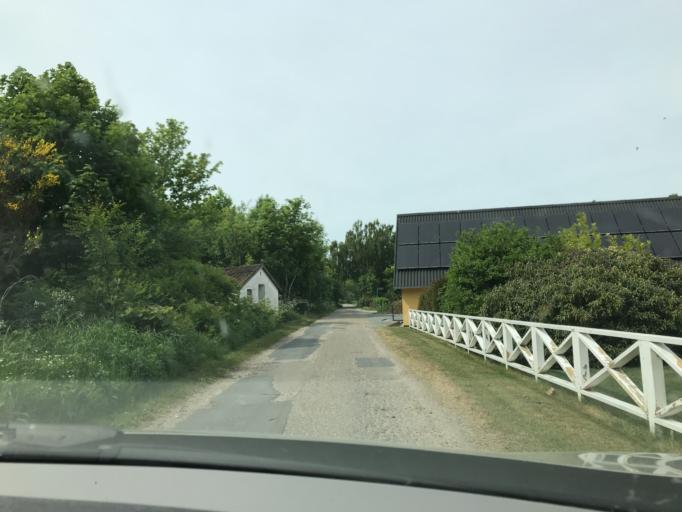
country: DK
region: Central Jutland
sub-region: Norddjurs Kommune
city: Allingabro
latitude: 56.5942
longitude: 10.3183
